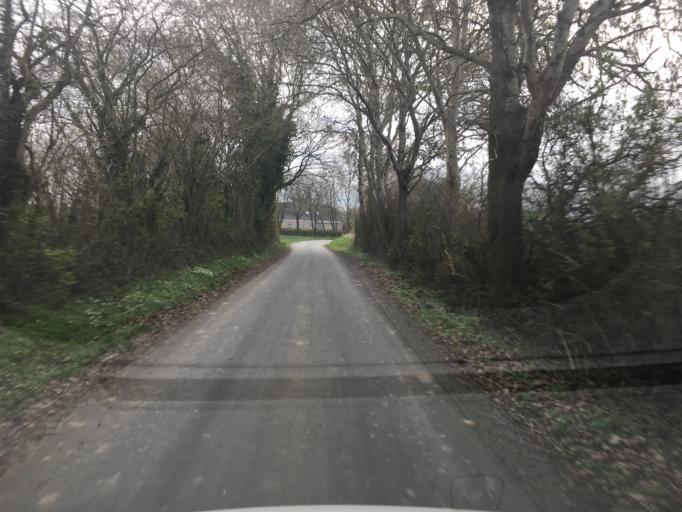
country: DE
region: Schleswig-Holstein
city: Glucksburg
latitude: 54.9012
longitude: 9.5254
